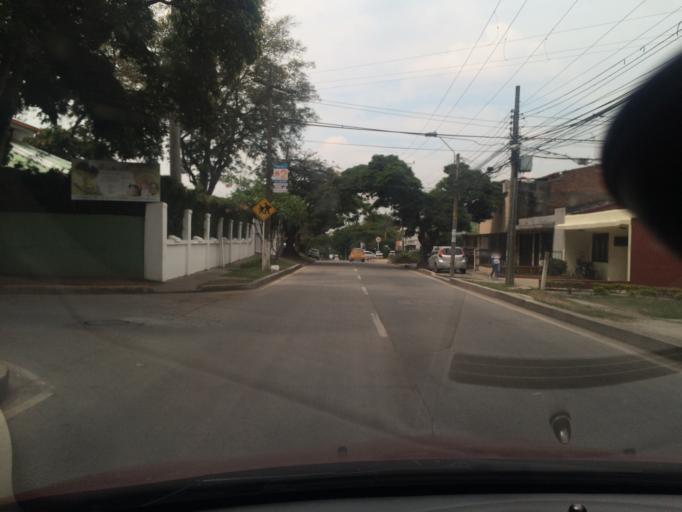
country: CO
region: Valle del Cauca
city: Cali
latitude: 3.4280
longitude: -76.5483
